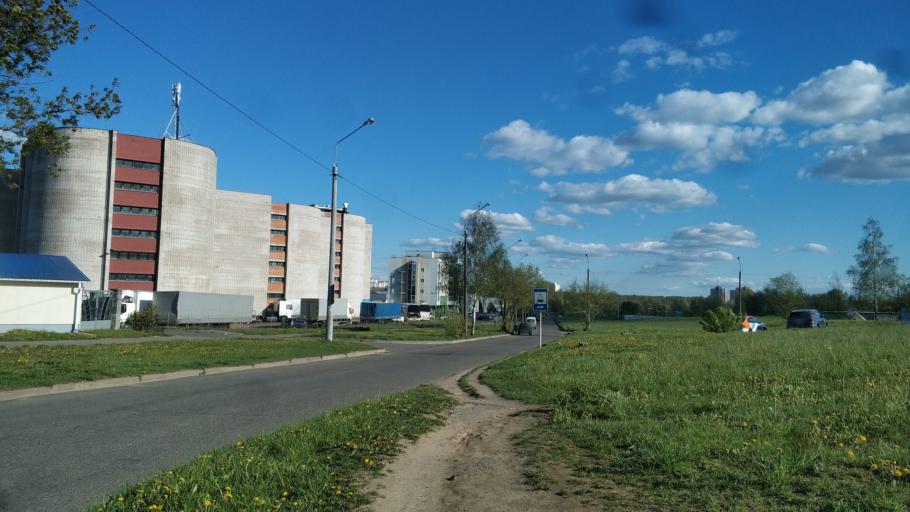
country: BY
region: Minsk
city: Minsk
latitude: 53.8802
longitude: 27.5817
